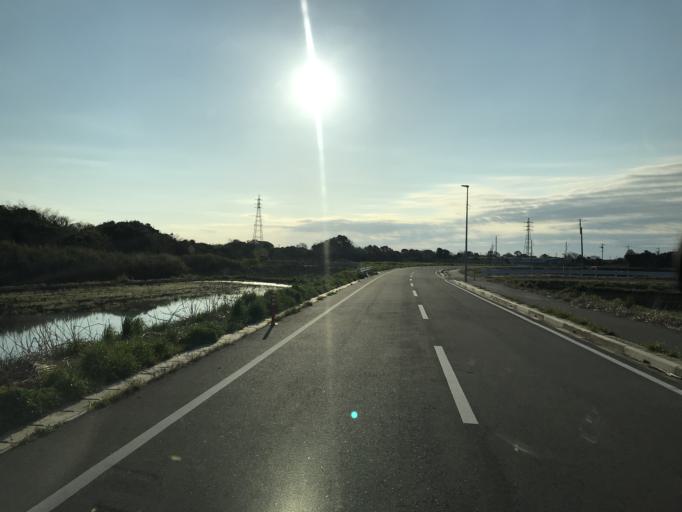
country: JP
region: Chiba
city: Yokaichiba
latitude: 35.6822
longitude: 140.5749
